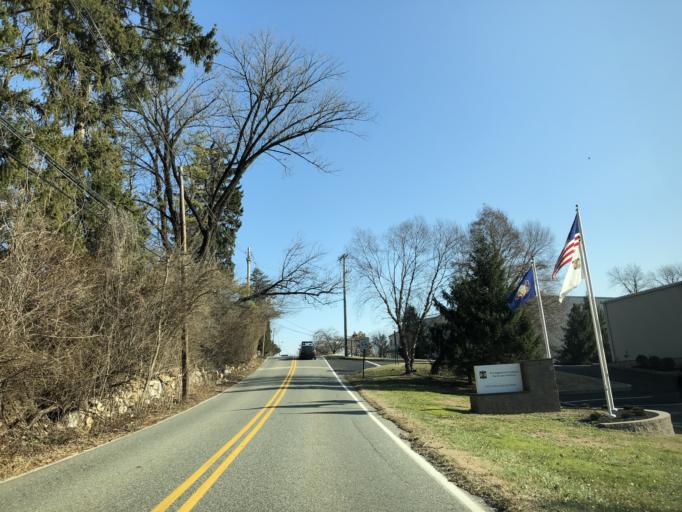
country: US
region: Pennsylvania
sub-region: Chester County
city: Malvern
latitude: 40.0727
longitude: -75.5193
